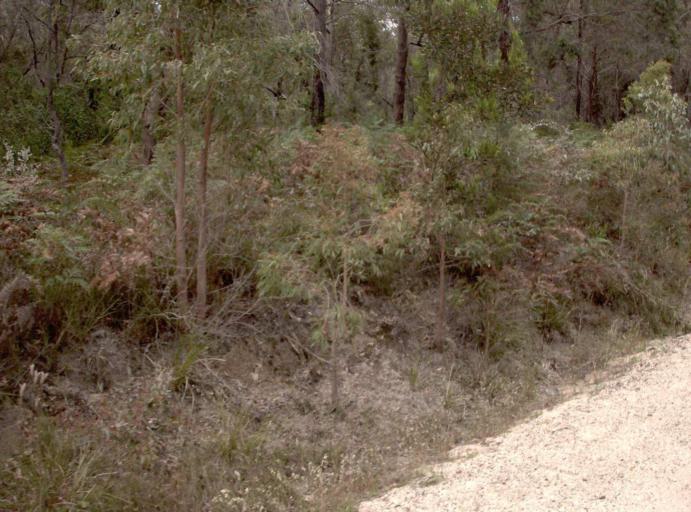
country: AU
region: New South Wales
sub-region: Bega Valley
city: Eden
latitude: -37.4051
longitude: 149.6647
